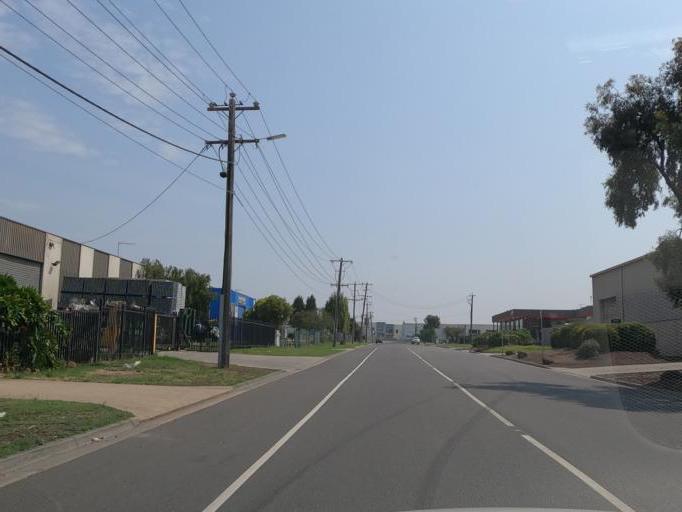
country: AU
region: Victoria
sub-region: Hume
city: Coolaroo
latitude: -37.6474
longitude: 144.9466
